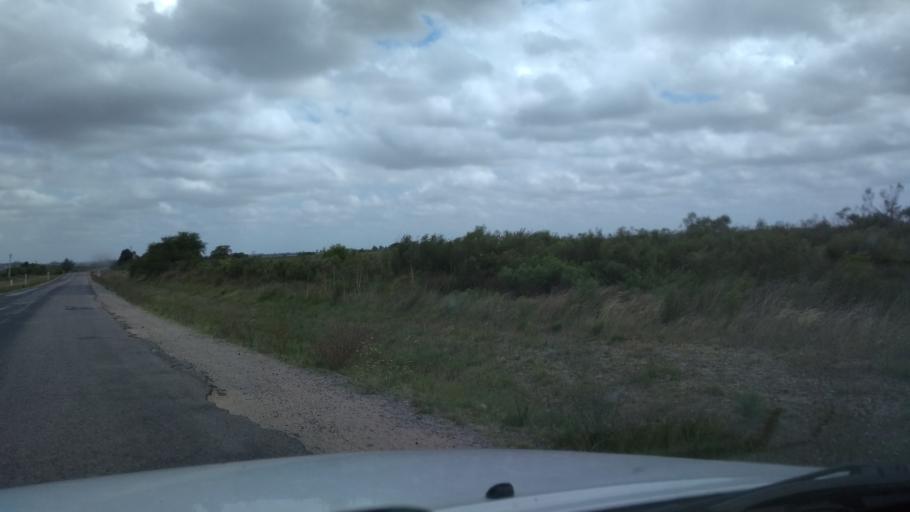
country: UY
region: Canelones
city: San Ramon
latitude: -34.2601
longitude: -55.9271
